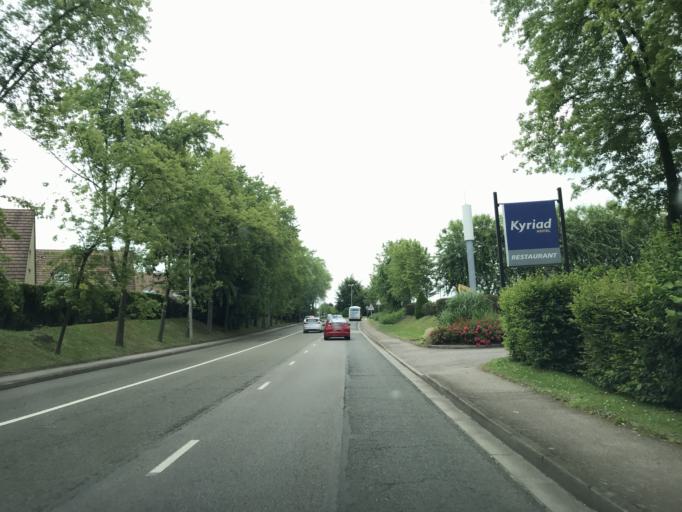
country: FR
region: Haute-Normandie
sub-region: Departement de la Seine-Maritime
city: Mont-Saint-Aignan
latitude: 49.4695
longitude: 1.0906
